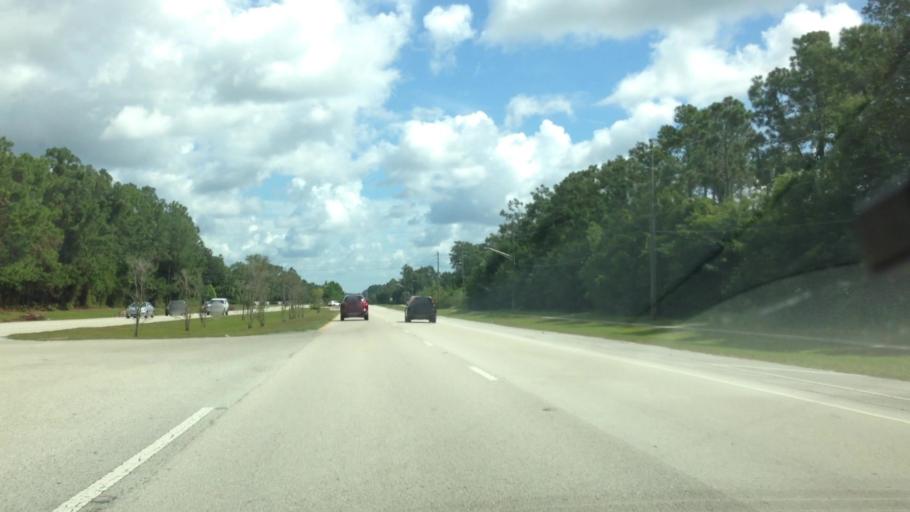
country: US
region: Florida
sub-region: Duval County
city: Jacksonville Beach
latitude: 30.2691
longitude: -81.4641
